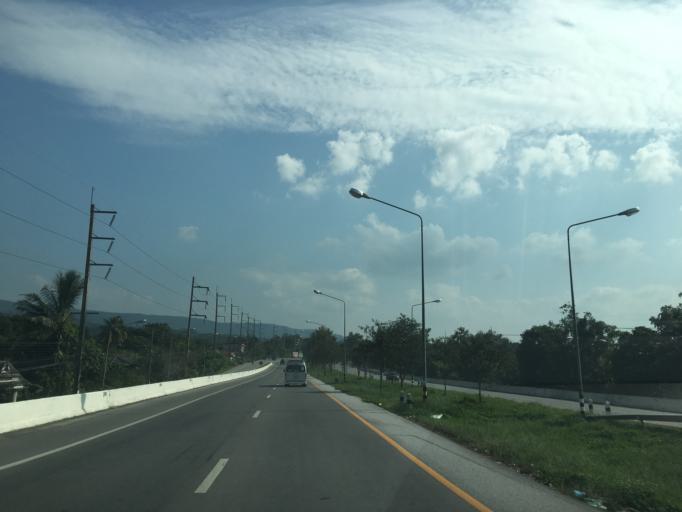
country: TH
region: Chiang Rai
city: Mae Lao
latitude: 19.7141
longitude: 99.7183
